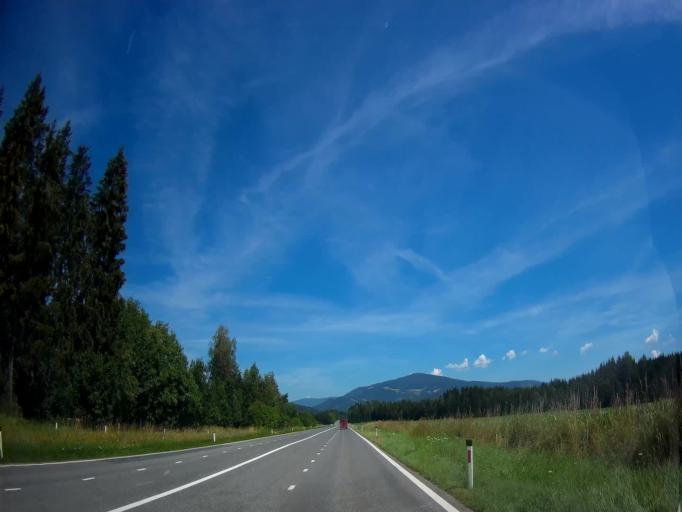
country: AT
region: Carinthia
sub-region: Politischer Bezirk Sankt Veit an der Glan
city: Molbling
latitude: 46.8471
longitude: 14.4481
